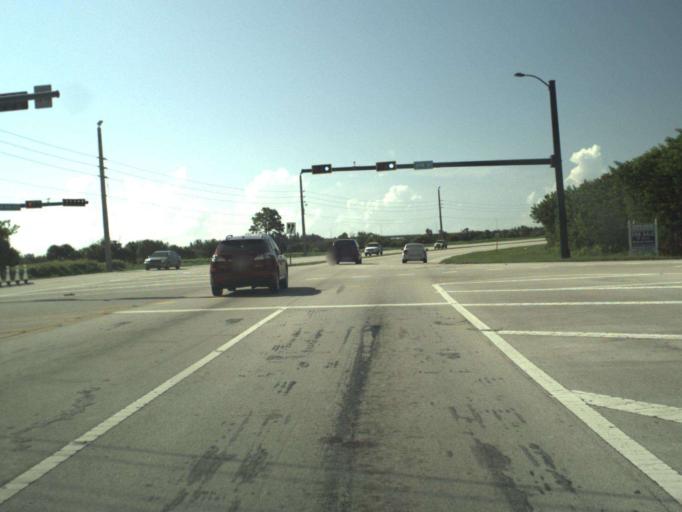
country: US
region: Florida
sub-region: Indian River County
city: Vero Beach
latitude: 27.6605
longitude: -80.3862
